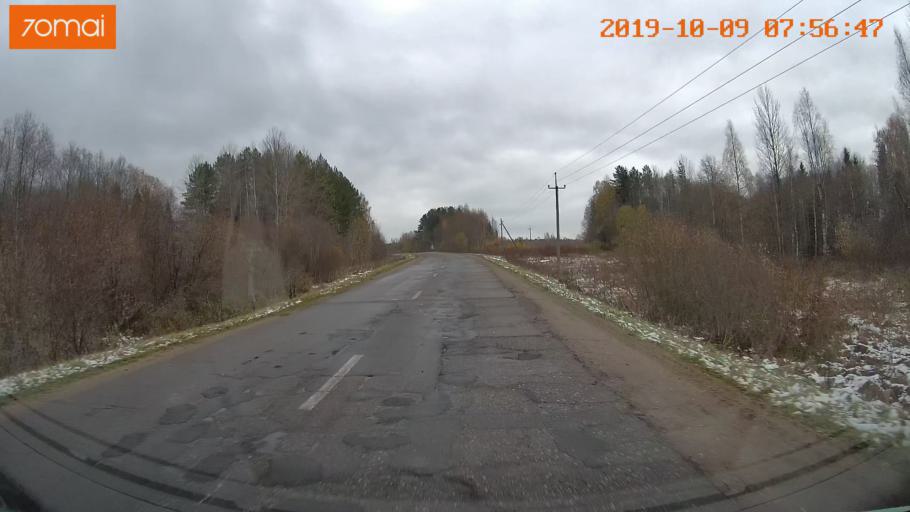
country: RU
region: Jaroslavl
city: Kukoboy
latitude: 58.6973
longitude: 39.9406
